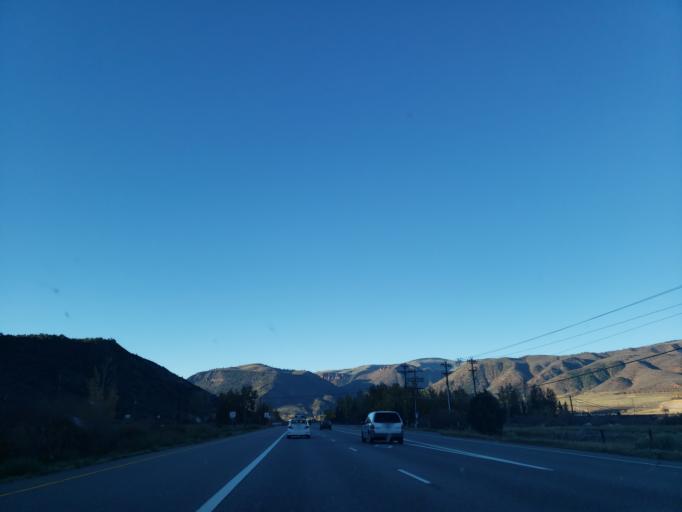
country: US
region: Colorado
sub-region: Pitkin County
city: Snowmass Village
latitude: 39.2594
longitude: -106.8872
